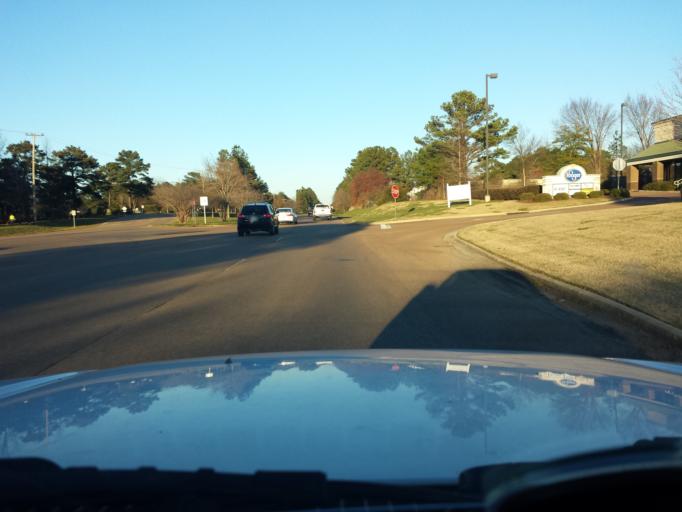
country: US
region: Mississippi
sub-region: Madison County
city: Ridgeland
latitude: 32.3840
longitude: -90.0406
